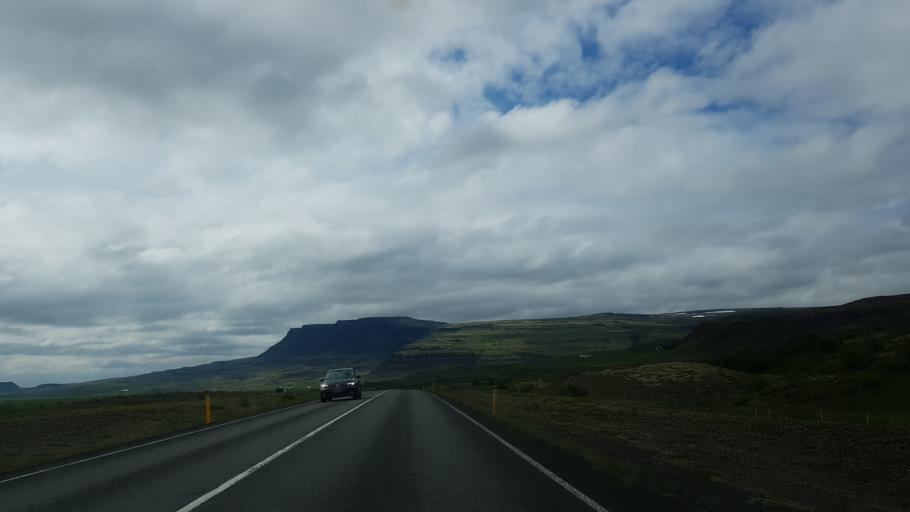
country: IS
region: West
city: Borgarnes
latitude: 64.8051
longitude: -21.4323
